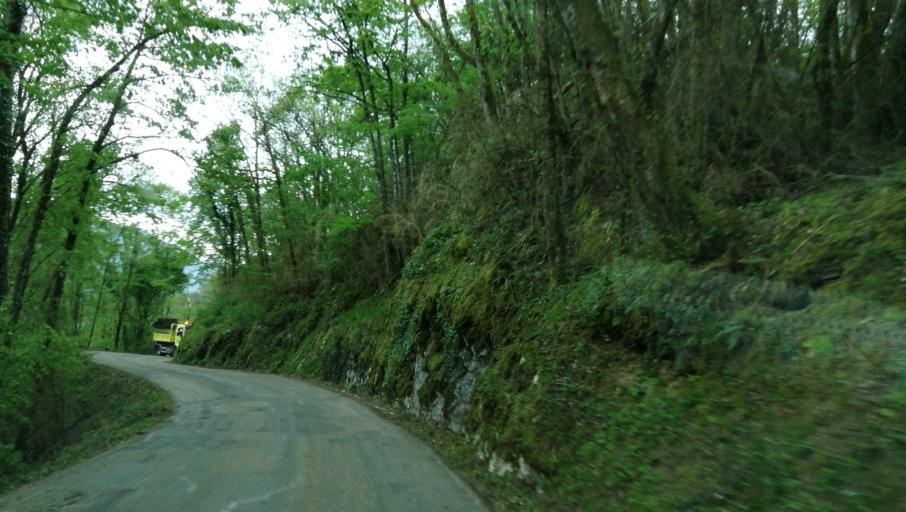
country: FR
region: Rhone-Alpes
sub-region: Departement de la Savoie
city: Brison-Saint-Innocent
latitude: 45.7309
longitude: 5.8442
